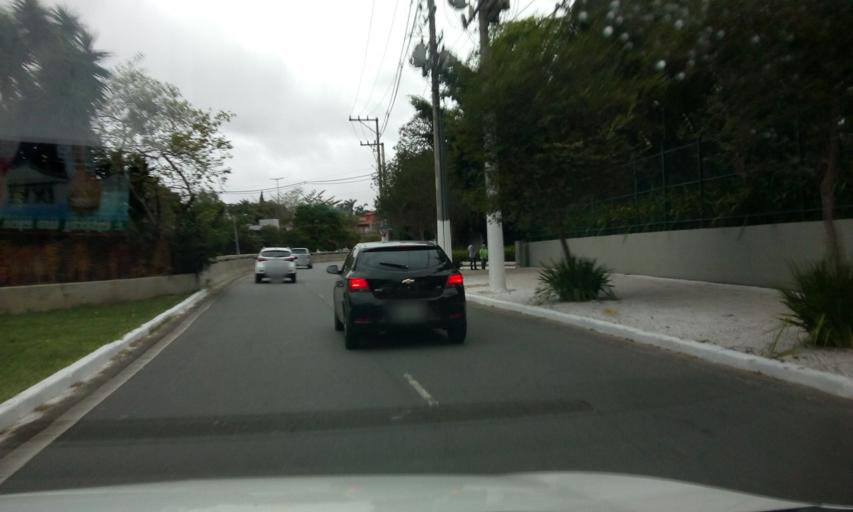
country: BR
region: Sao Paulo
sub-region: Sao Paulo
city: Sao Paulo
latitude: -23.5854
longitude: -46.6693
